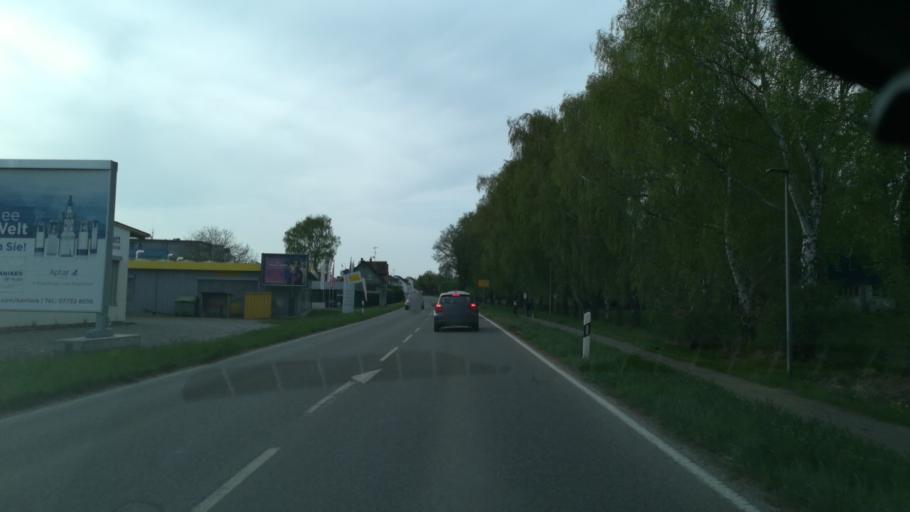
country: DE
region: Baden-Wuerttemberg
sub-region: Freiburg Region
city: Moos
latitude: 47.7503
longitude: 8.9461
